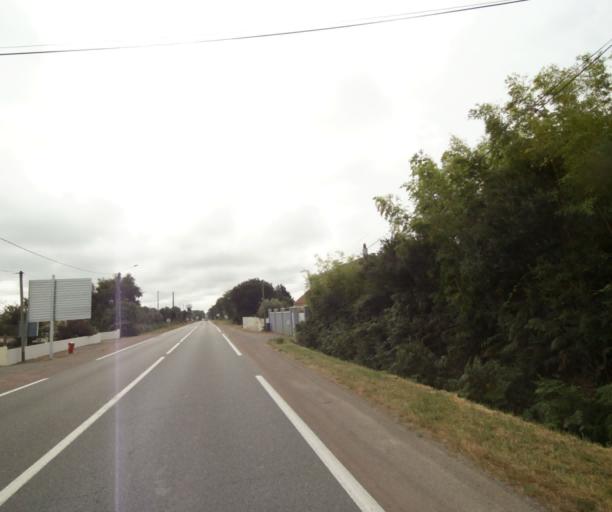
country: FR
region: Pays de la Loire
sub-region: Departement de la Vendee
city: Chateau-d'Olonne
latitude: 46.4813
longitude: -1.7139
